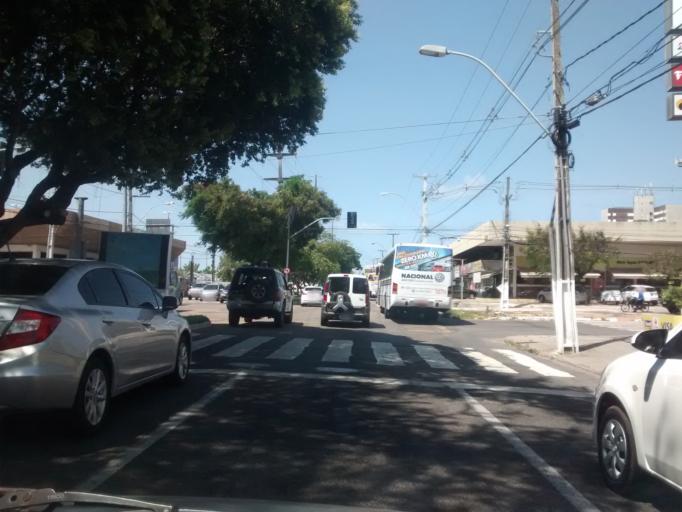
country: BR
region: Rio Grande do Norte
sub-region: Natal
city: Natal
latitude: -5.8167
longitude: -35.2118
